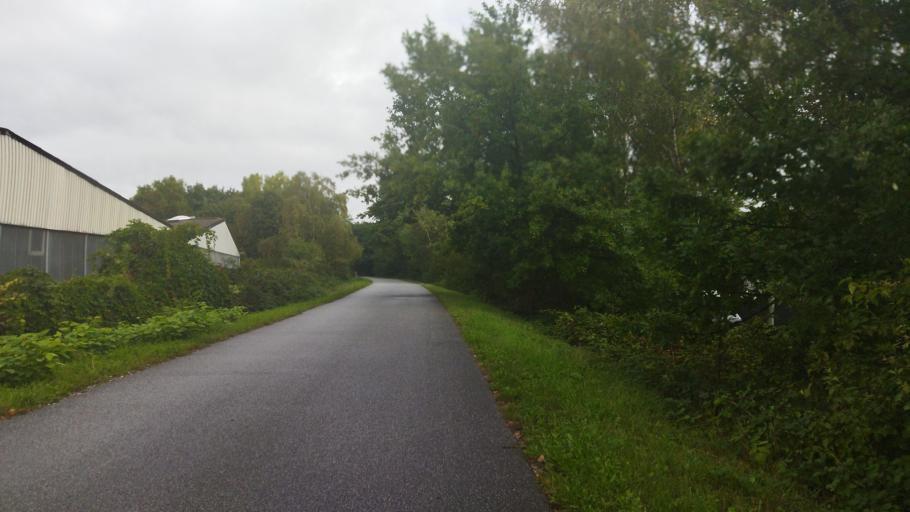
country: DE
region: North Rhine-Westphalia
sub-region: Regierungsbezirk Munster
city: Gelsenkirchen
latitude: 51.5040
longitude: 7.1312
